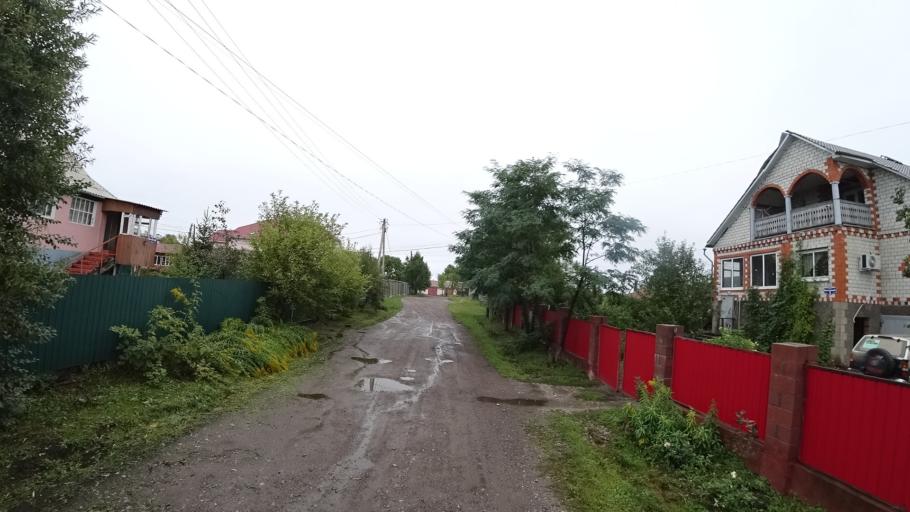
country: RU
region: Primorskiy
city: Monastyrishche
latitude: 44.2007
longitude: 132.4479
